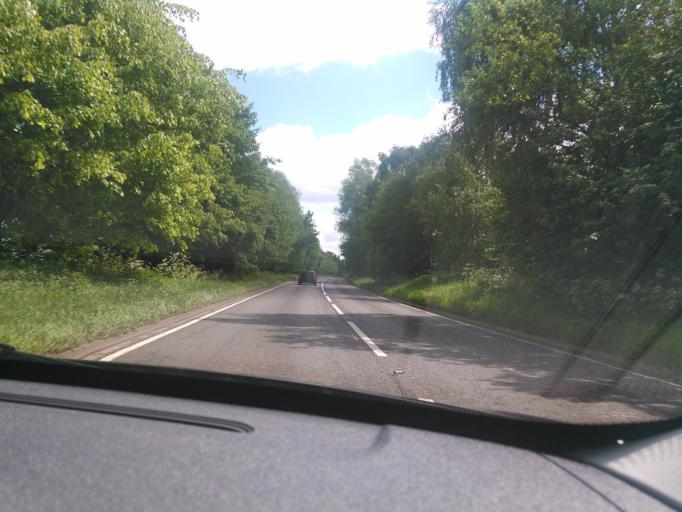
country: GB
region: England
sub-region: Shropshire
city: Market Drayton
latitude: 52.9118
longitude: -2.4803
